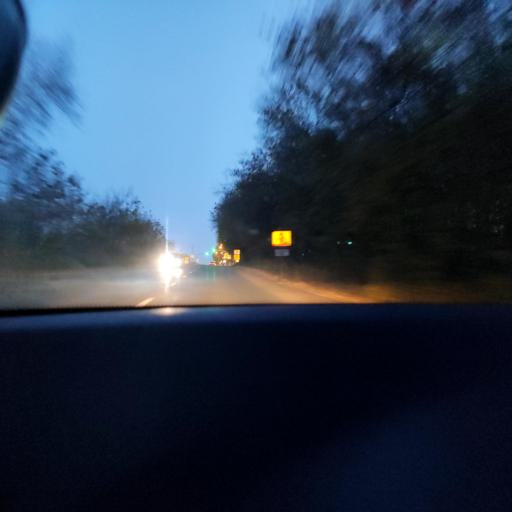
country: RU
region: Samara
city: Petra-Dubrava
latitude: 53.3097
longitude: 50.2764
